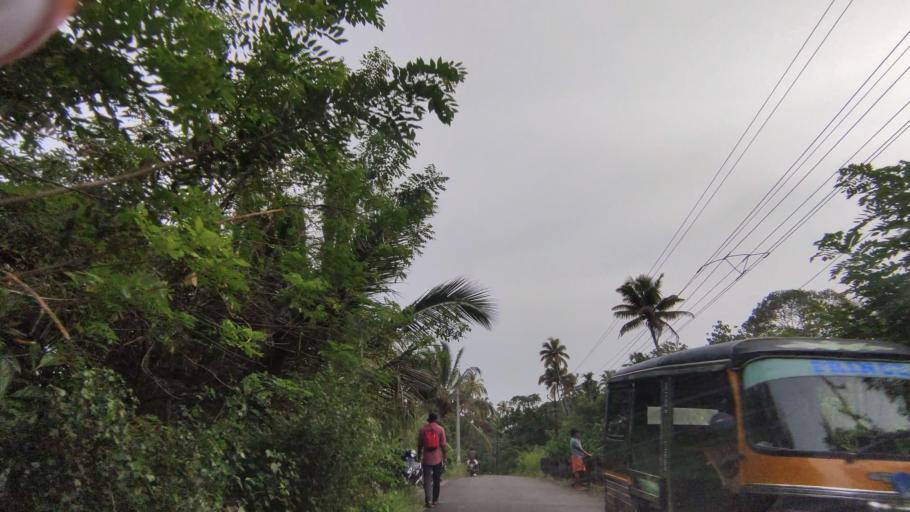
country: IN
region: Kerala
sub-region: Alappuzha
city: Shertallai
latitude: 9.6733
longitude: 76.3700
